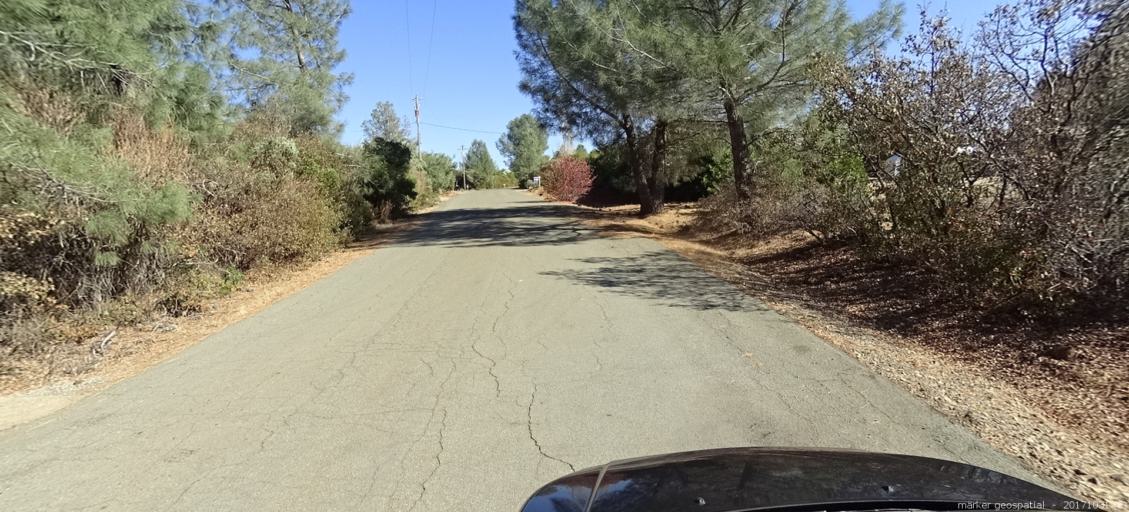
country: US
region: California
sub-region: Shasta County
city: Shingletown
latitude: 40.5083
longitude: -122.0221
